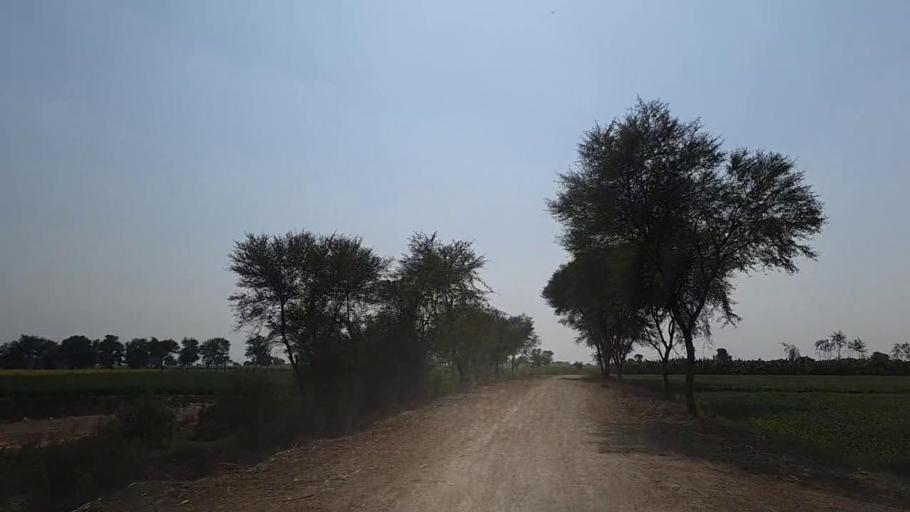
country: PK
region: Sindh
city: Daur
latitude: 26.4899
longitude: 68.2599
